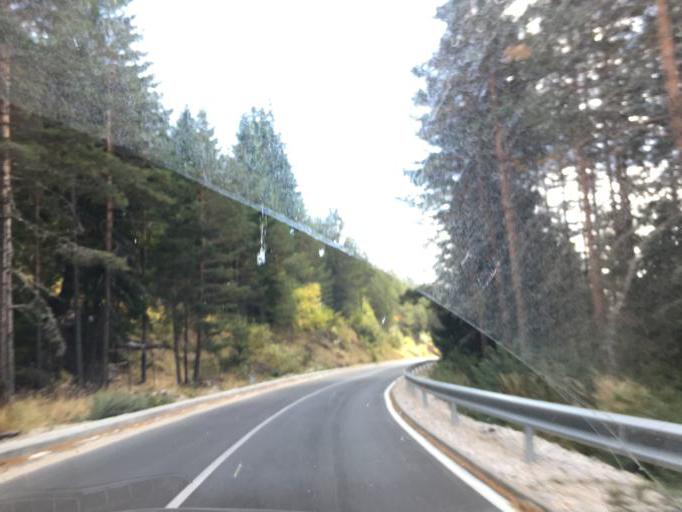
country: BG
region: Pazardzhik
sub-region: Obshtina Batak
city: Batak
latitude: 41.8969
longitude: 24.3187
